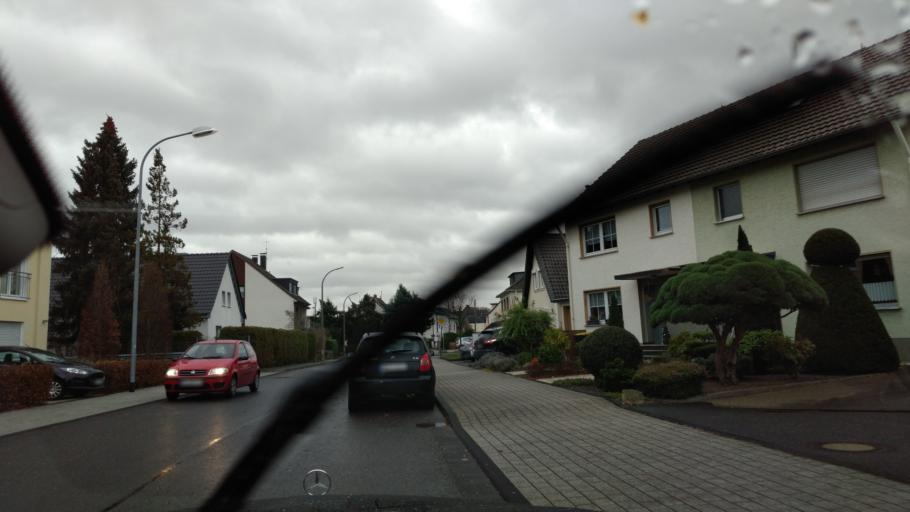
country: DE
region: North Rhine-Westphalia
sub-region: Regierungsbezirk Koln
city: Bonn
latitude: 50.7777
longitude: 7.0934
